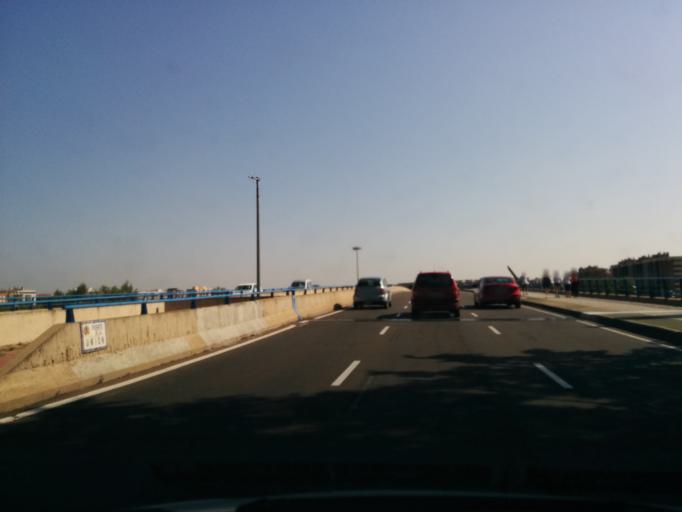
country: ES
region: Aragon
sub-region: Provincia de Zaragoza
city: Zaragoza
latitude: 41.6513
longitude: -0.8632
